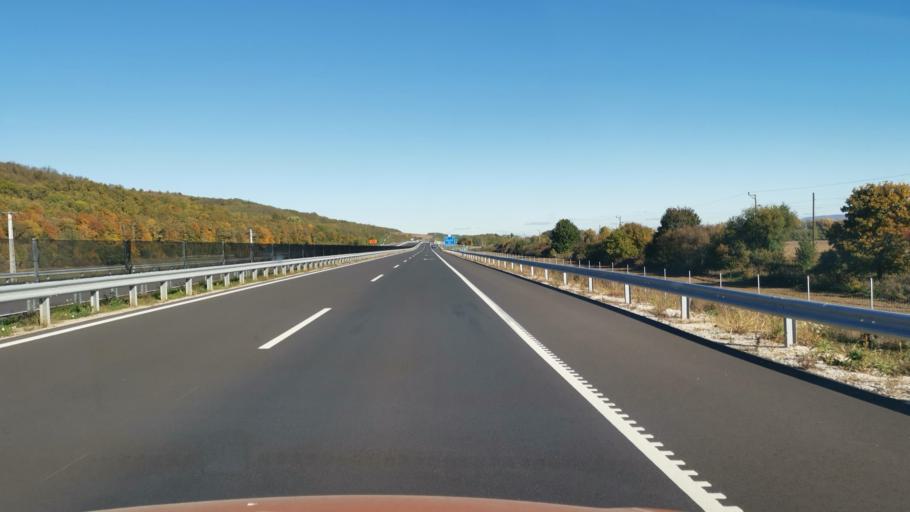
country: HU
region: Borsod-Abauj-Zemplen
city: Gonc
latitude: 48.4643
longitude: 21.1999
